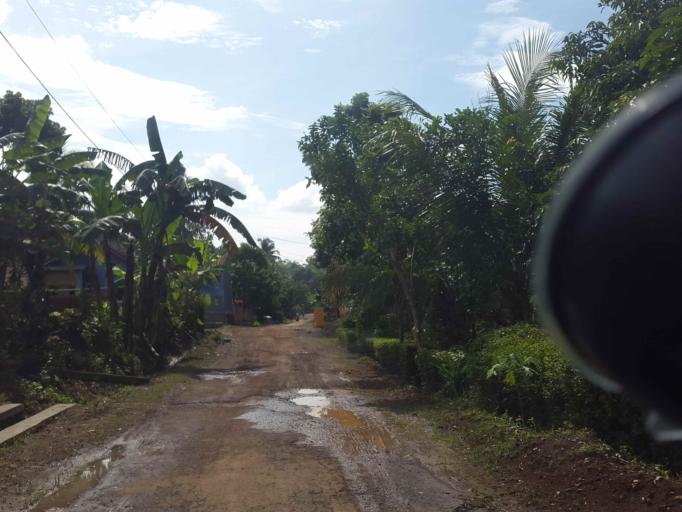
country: ID
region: Central Java
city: Garbi
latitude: -7.4581
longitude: 109.1923
